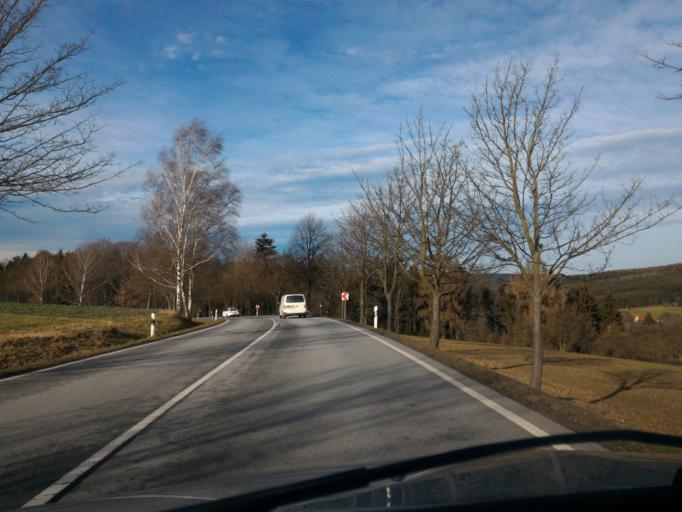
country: DE
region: Saxony
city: Sohland
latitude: 51.0555
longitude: 14.4212
